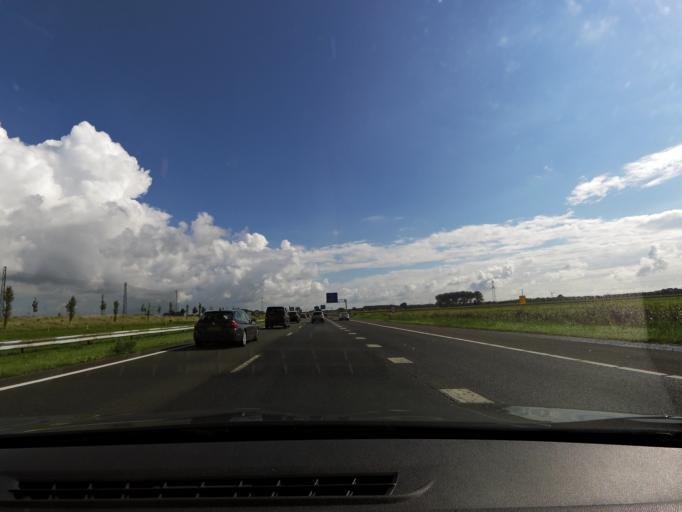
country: NL
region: Zeeland
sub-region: Gemeente Middelburg
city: Middelburg
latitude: 51.4775
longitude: 3.6397
